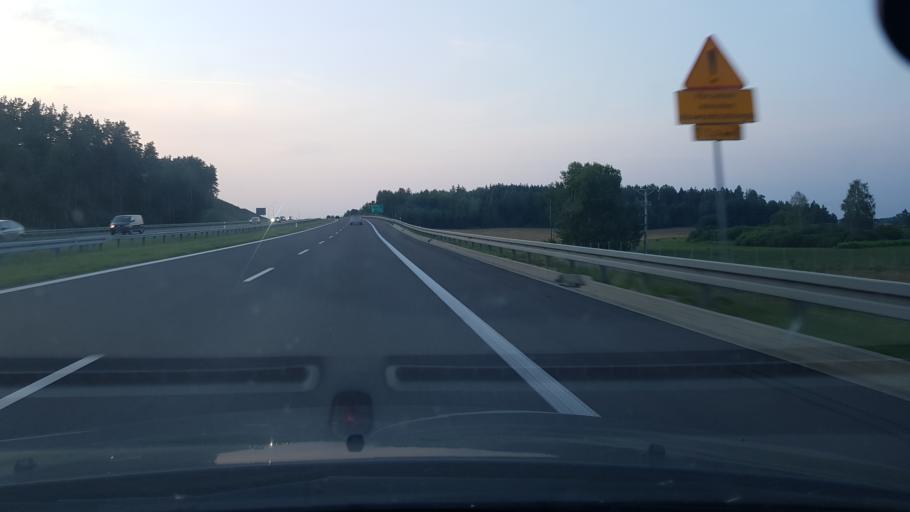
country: PL
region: Warmian-Masurian Voivodeship
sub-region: Powiat nidzicki
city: Nidzica
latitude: 53.3629
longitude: 20.3899
